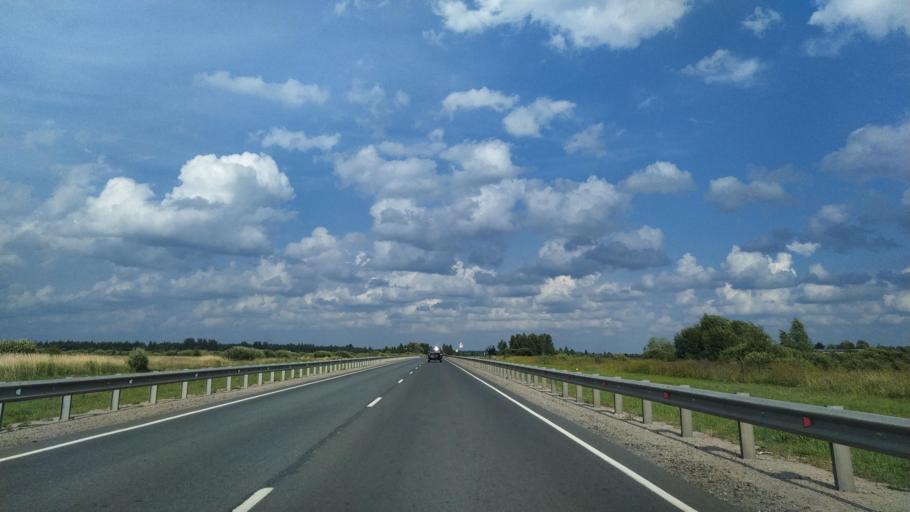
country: RU
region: Novgorod
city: Sol'tsy
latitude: 58.1303
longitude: 30.3644
